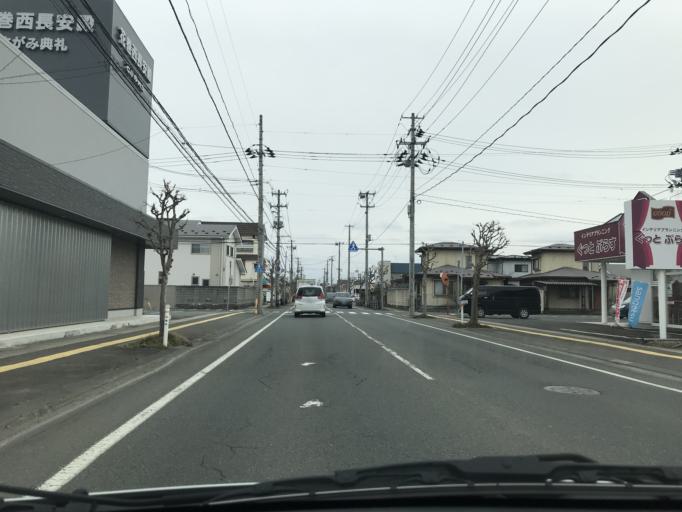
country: JP
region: Iwate
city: Hanamaki
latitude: 39.3919
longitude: 141.1080
